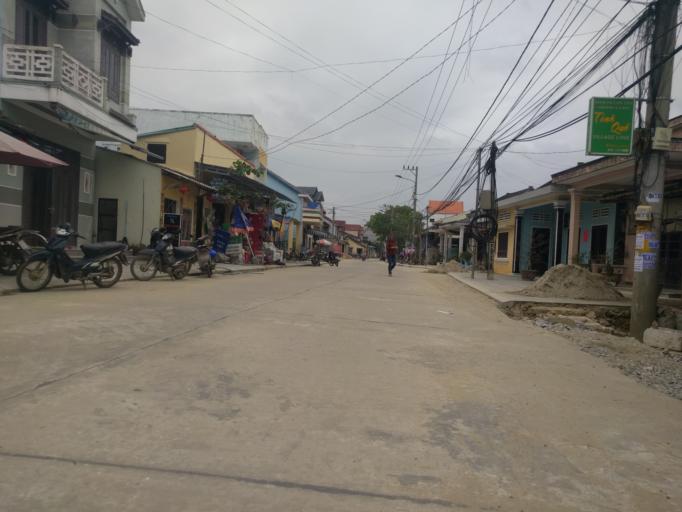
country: VN
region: Quang Nam
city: Hoi An
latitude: 15.8712
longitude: 108.3460
